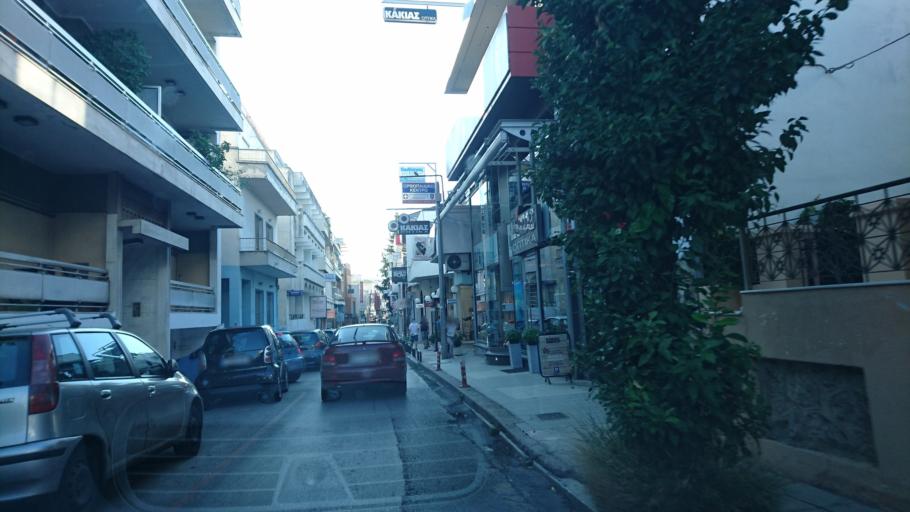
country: GR
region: Attica
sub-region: Nomarchia Athinas
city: Khalandrion
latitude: 38.0214
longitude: 23.8027
